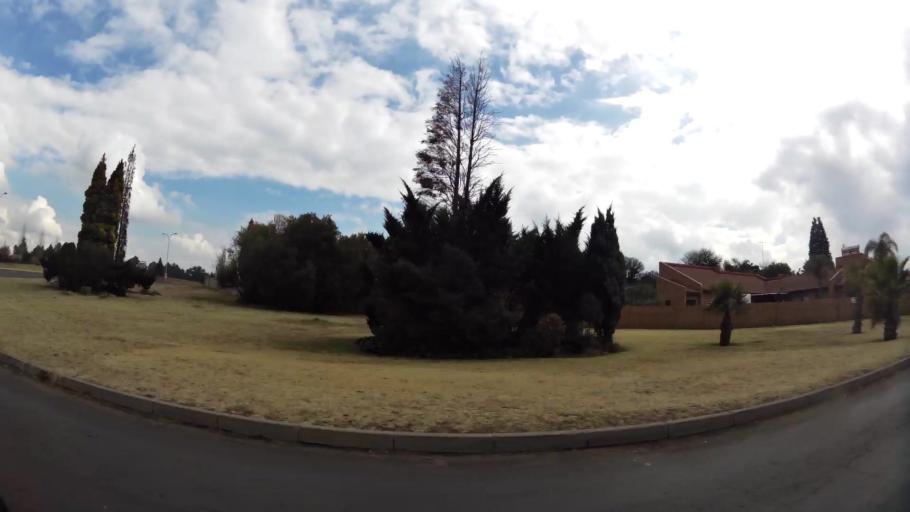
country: ZA
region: Gauteng
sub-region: Sedibeng District Municipality
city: Vanderbijlpark
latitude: -26.7429
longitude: 27.8545
